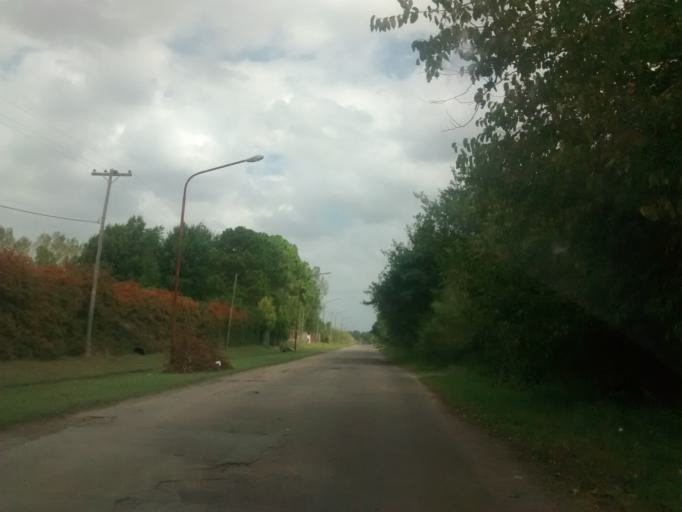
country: AR
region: Buenos Aires
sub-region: Partido de La Plata
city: La Plata
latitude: -34.9997
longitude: -57.9057
